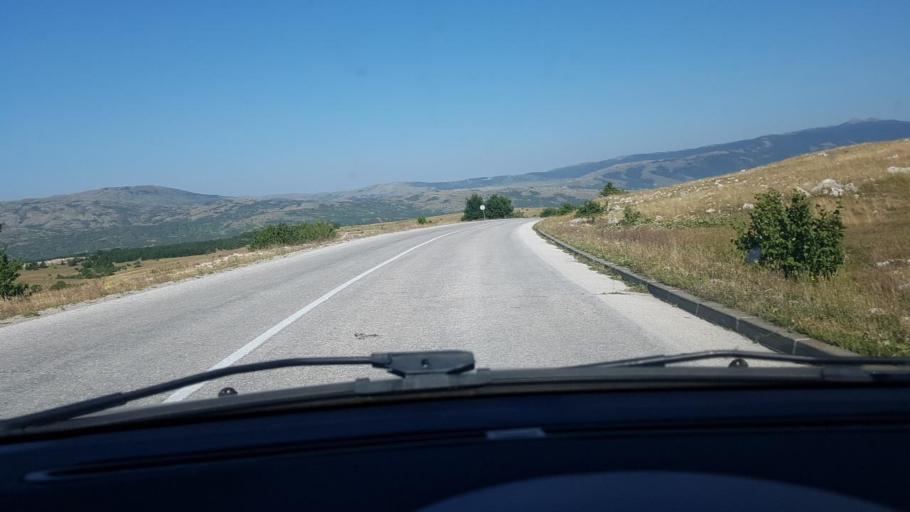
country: BA
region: Federation of Bosnia and Herzegovina
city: Tomislavgrad
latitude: 43.7880
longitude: 17.2464
